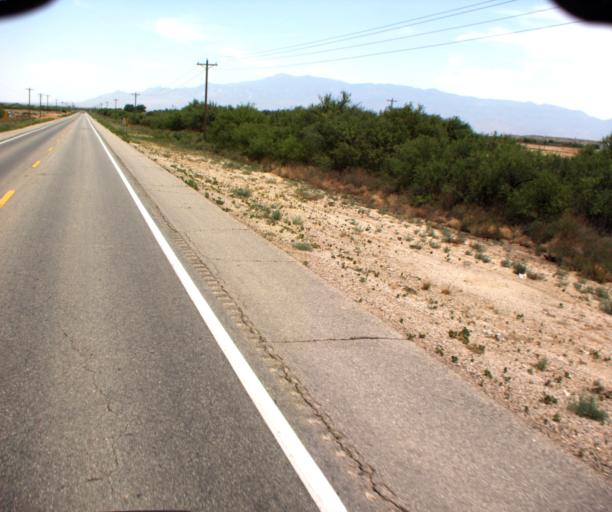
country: US
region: Arizona
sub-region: Graham County
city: Pima
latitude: 32.9588
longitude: -109.9185
